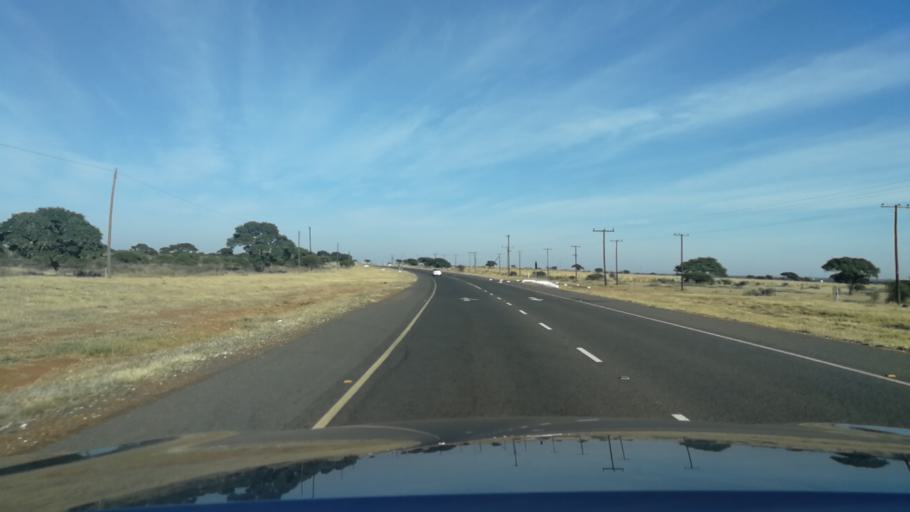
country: BW
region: South East
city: Janeng
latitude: -25.4749
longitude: 25.5210
